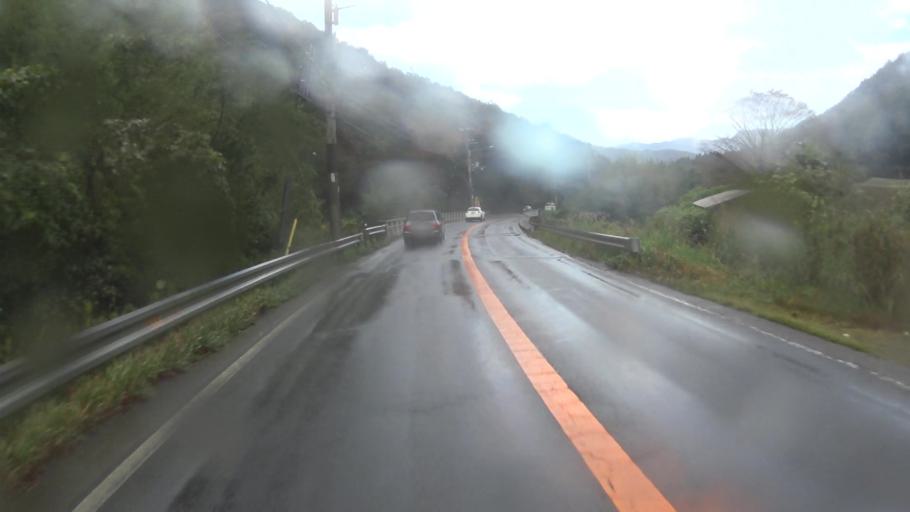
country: JP
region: Kyoto
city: Ayabe
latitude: 35.1931
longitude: 135.2877
